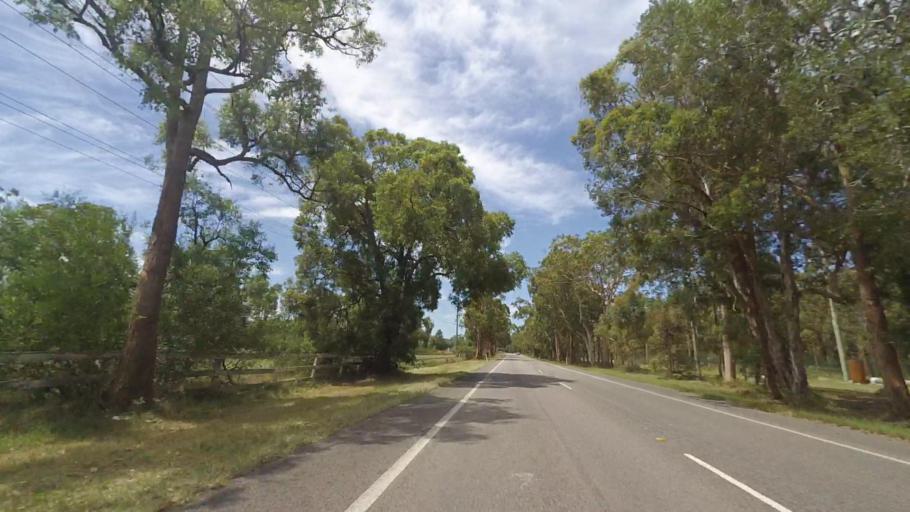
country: AU
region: New South Wales
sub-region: Port Stephens Shire
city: Medowie
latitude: -32.7688
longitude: 151.8621
